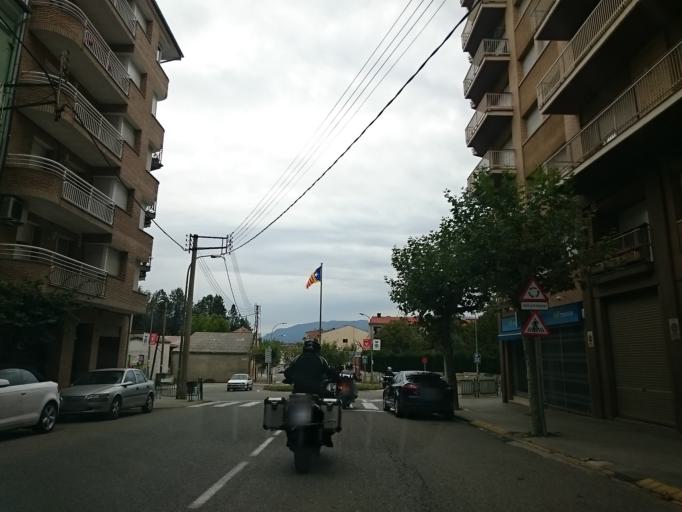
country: ES
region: Catalonia
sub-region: Provincia de Lleida
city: Tremp
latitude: 42.1643
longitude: 0.8947
